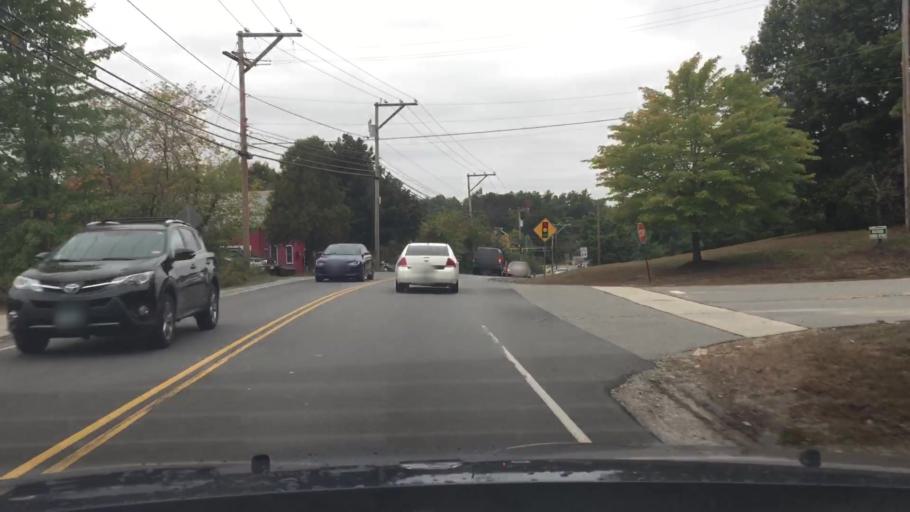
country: US
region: Massachusetts
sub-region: Middlesex County
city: Tyngsboro
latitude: 42.7176
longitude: -71.4167
